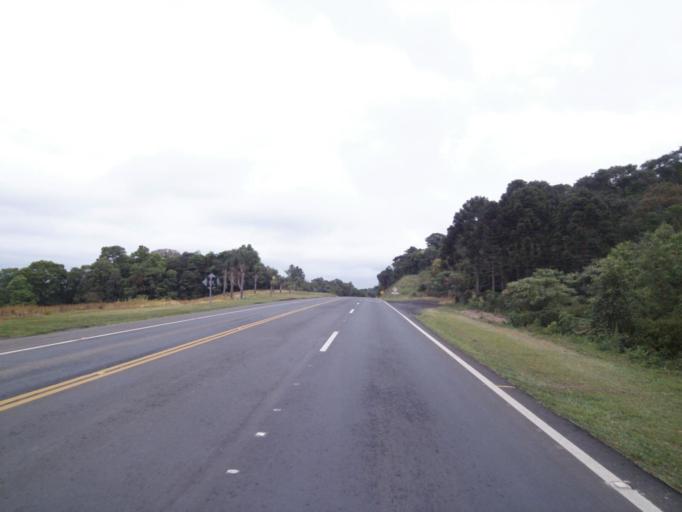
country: BR
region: Parana
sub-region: Irati
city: Irati
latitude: -25.4495
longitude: -50.6410
